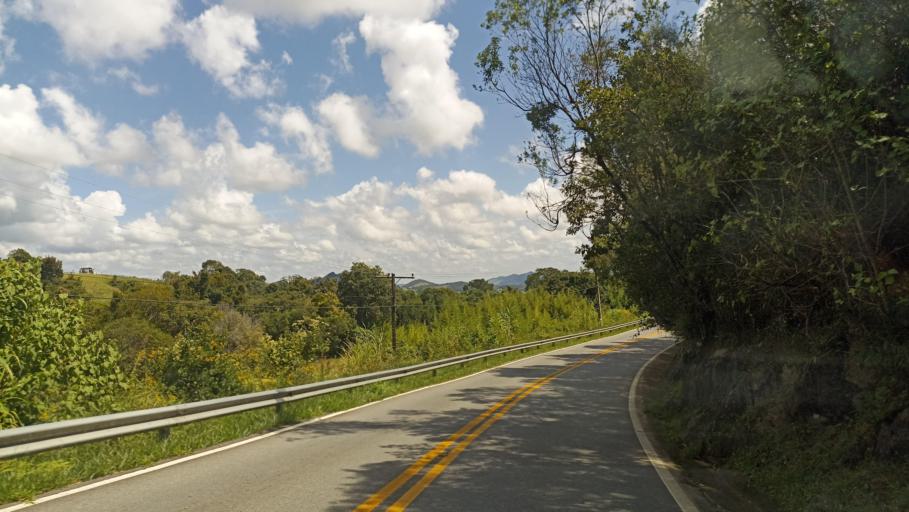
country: BR
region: Sao Paulo
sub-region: Cunha
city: Cunha
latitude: -23.1302
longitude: -44.9358
